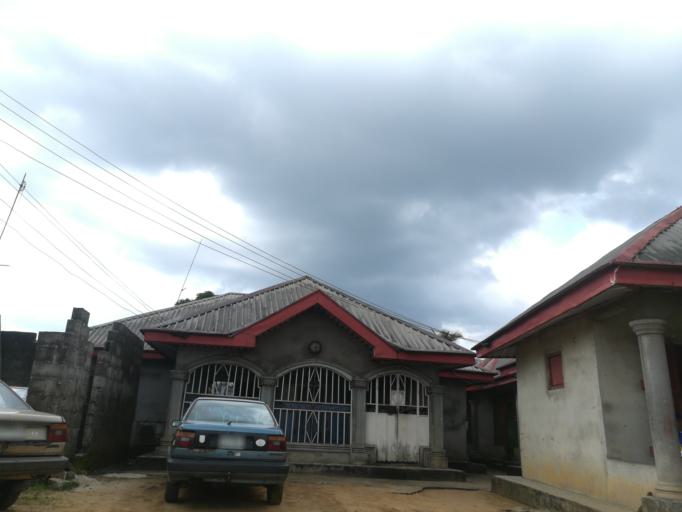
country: NG
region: Rivers
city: Okrika
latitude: 4.7314
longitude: 7.1449
